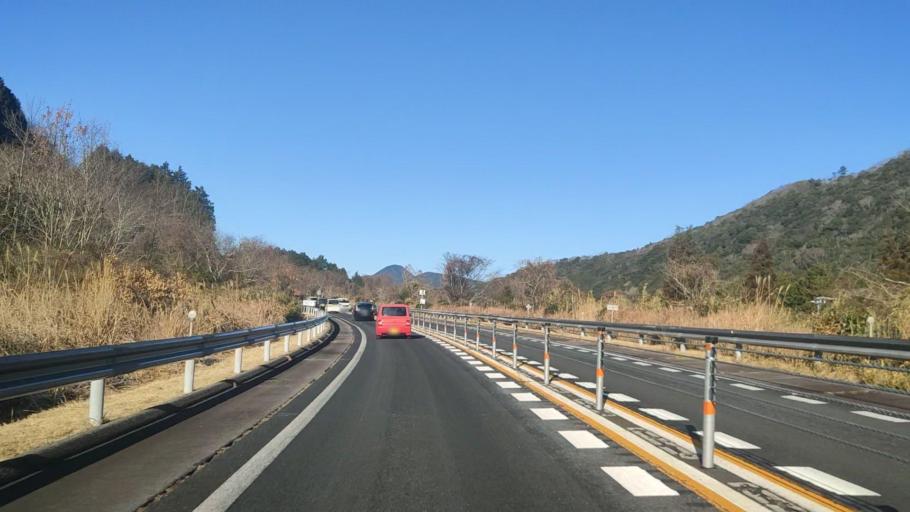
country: JP
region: Oita
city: Bungo-Takada-shi
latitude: 33.4573
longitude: 131.3570
